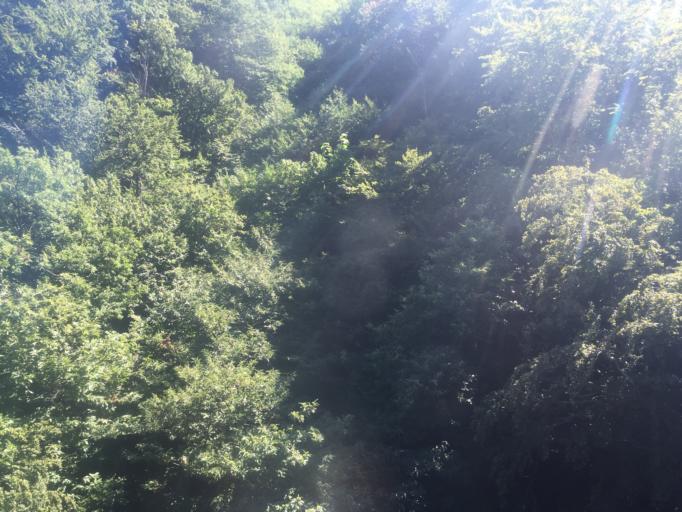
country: CH
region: Ticino
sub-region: Mendrisio District
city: Riva San Vitale
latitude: 45.9174
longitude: 8.9359
